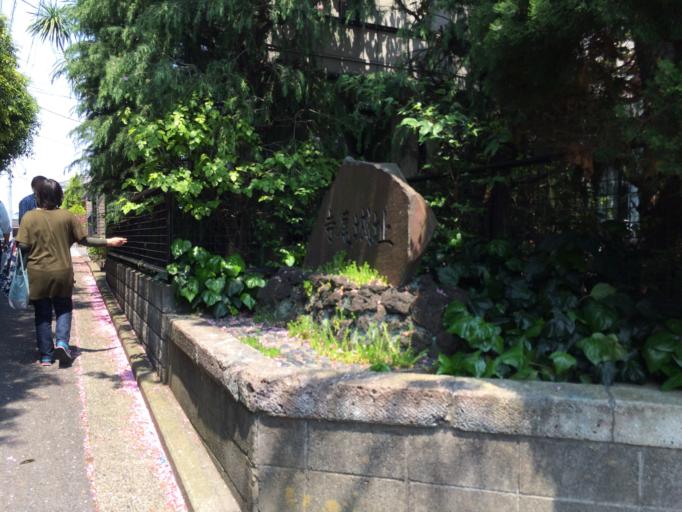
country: JP
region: Kanagawa
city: Yokohama
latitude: 35.5066
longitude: 139.6523
